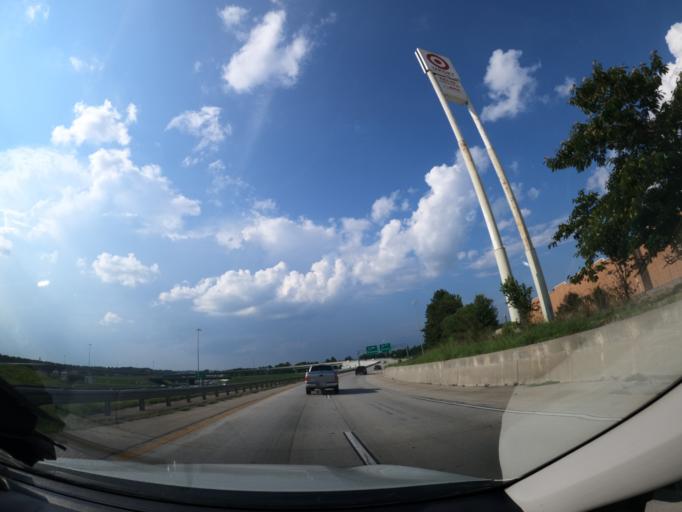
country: US
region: Georgia
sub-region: Columbia County
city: Martinez
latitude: 33.4905
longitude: -82.0827
